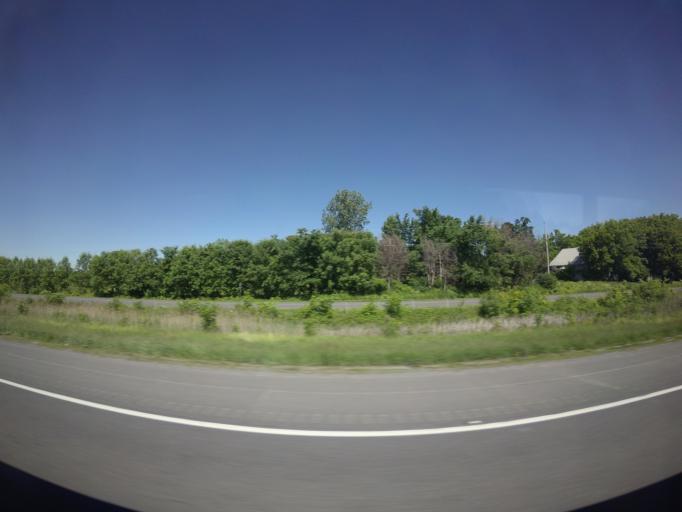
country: CA
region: Quebec
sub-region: Mauricie
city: Saint-Germain-de-Grantham
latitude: 45.7967
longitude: -72.6515
